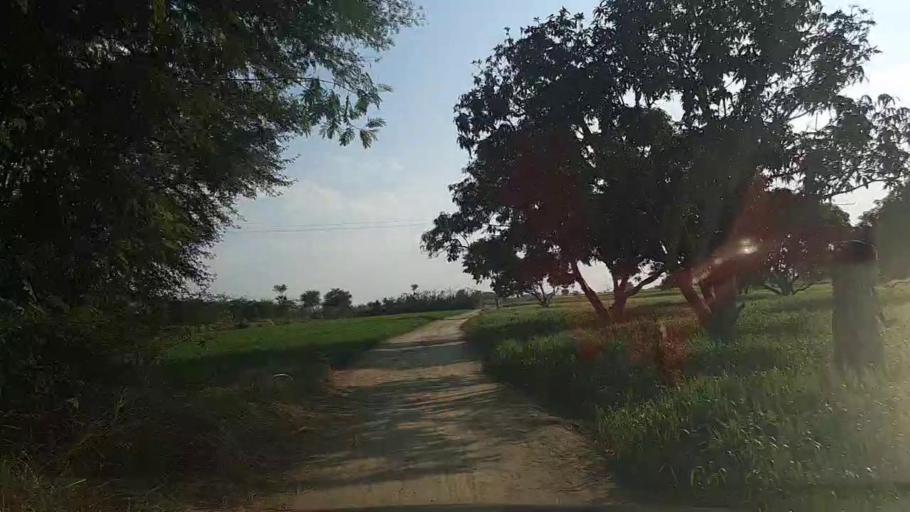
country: PK
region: Sindh
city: Jhol
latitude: 25.8350
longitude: 69.0516
